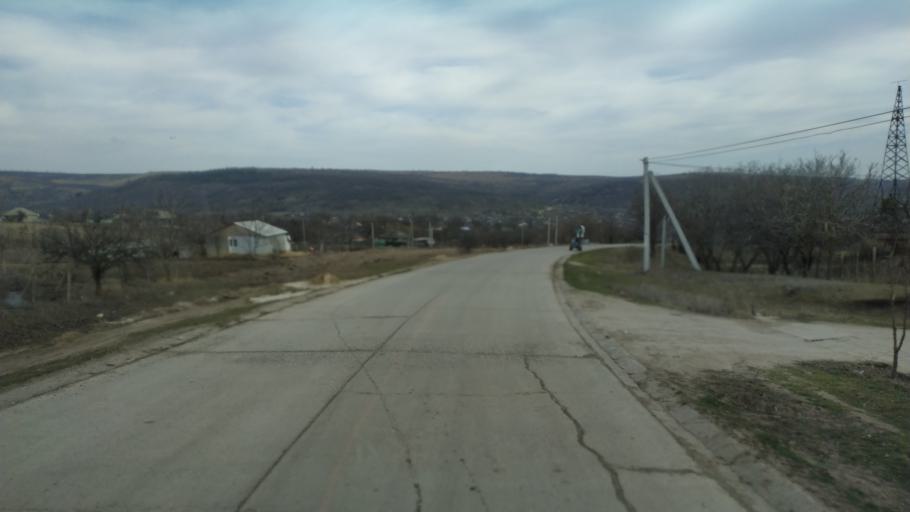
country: MD
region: Nisporeni
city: Nisporeni
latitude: 46.9290
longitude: 28.2579
